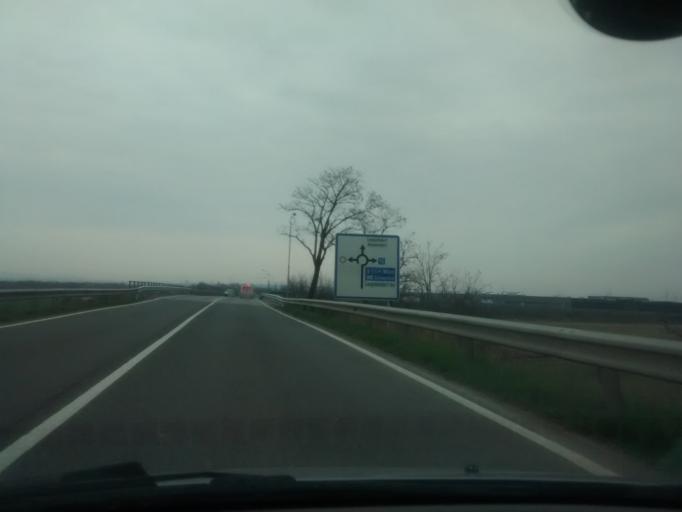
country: AT
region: Lower Austria
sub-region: Politischer Bezirk Modling
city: Achau
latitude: 48.0938
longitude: 16.3935
